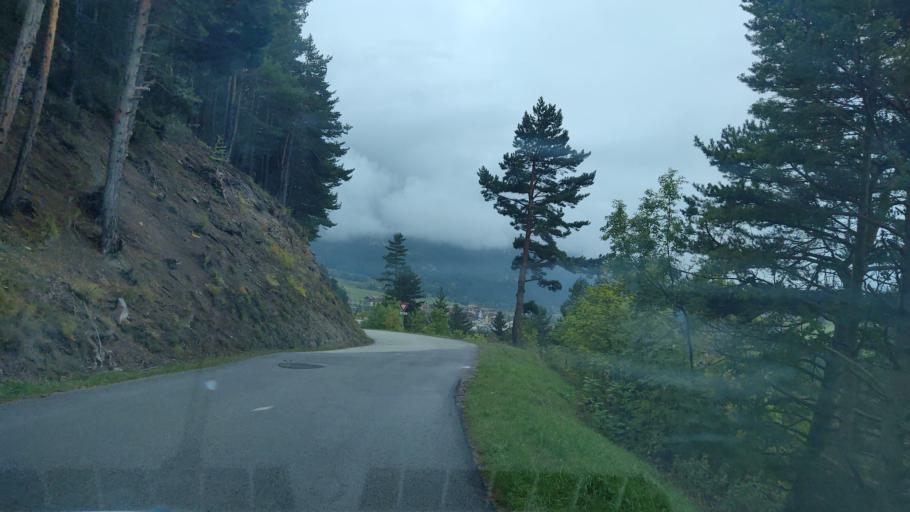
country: FR
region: Rhone-Alpes
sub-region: Departement de la Savoie
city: Modane
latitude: 45.2828
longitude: 6.8156
